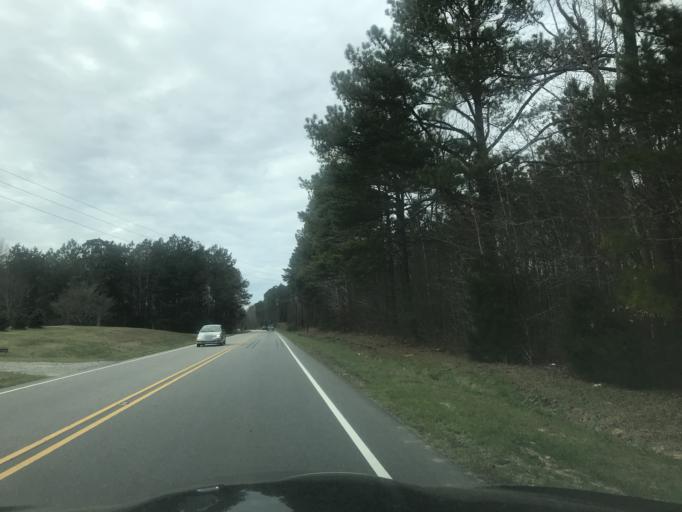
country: US
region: North Carolina
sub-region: Franklin County
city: Louisburg
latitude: 36.0838
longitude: -78.3477
